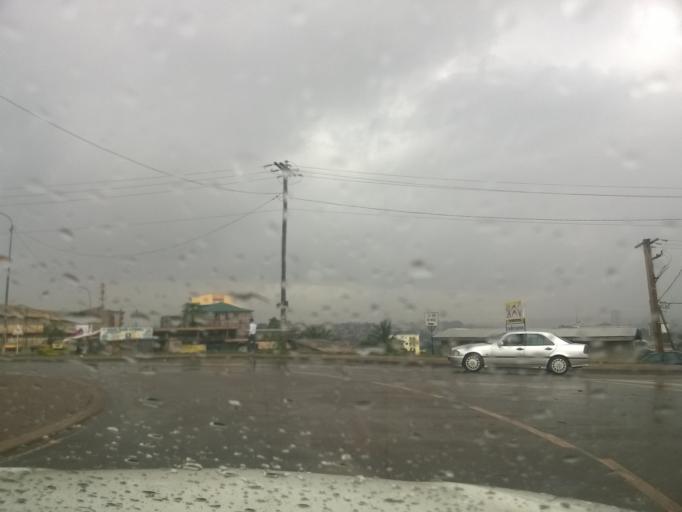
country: CM
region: Centre
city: Yaounde
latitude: 3.8849
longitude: 11.5387
